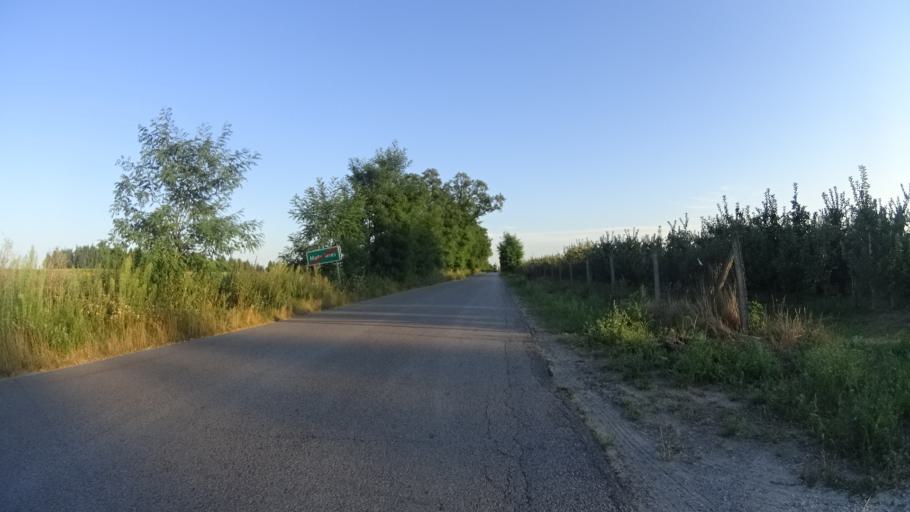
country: PL
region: Masovian Voivodeship
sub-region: Powiat bialobrzeski
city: Wysmierzyce
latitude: 51.6714
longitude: 20.8311
